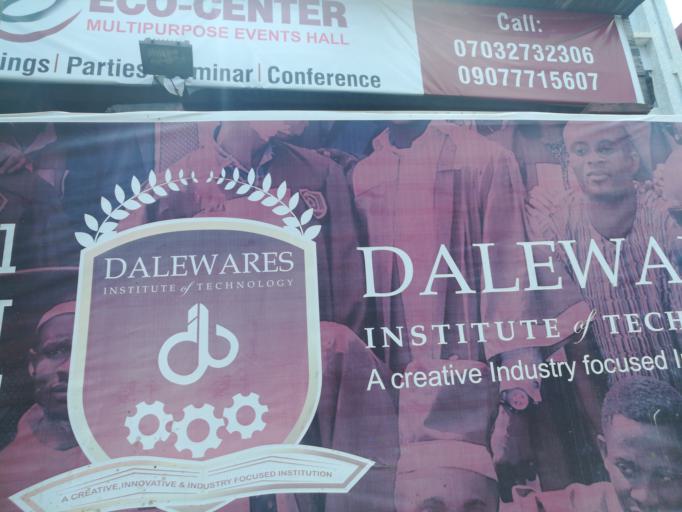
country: NG
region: Lagos
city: Somolu
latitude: 6.5375
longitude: 3.3665
